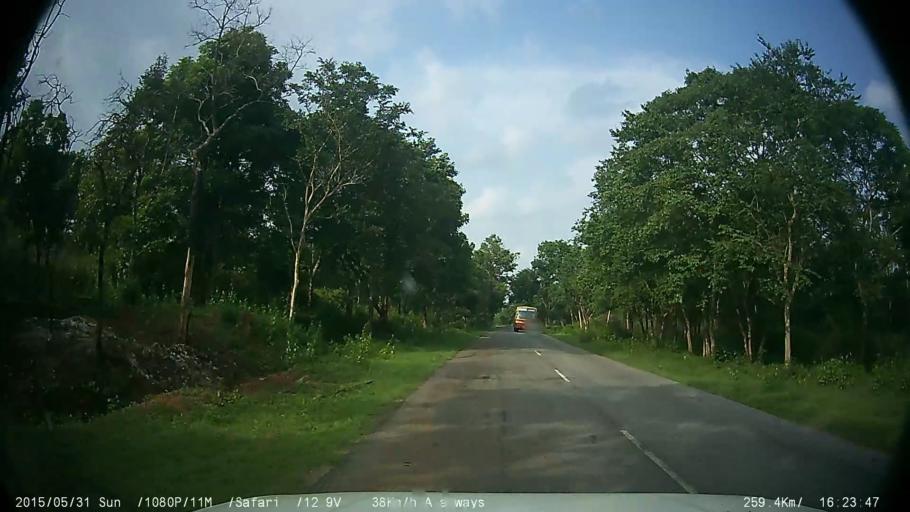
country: IN
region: Karnataka
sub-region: Chamrajnagar
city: Gundlupet
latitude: 11.7596
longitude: 76.5185
